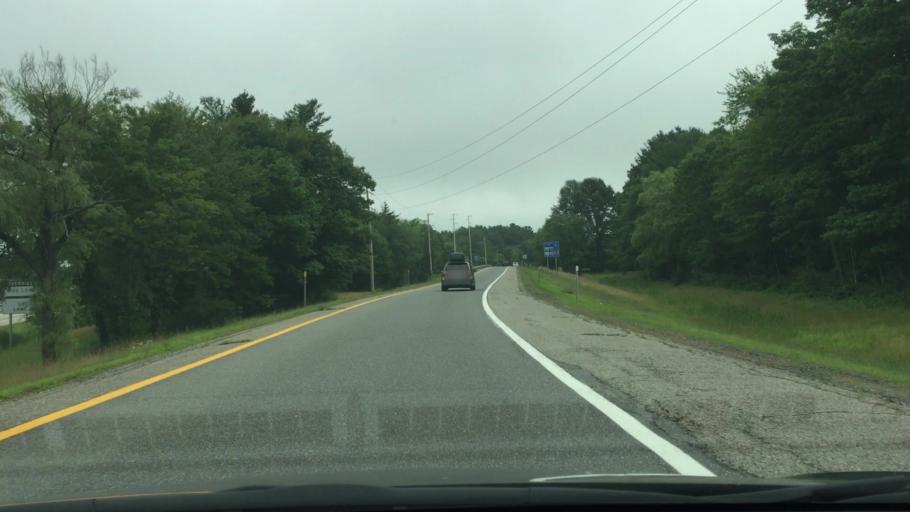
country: US
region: Maine
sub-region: York County
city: York Harbor
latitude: 43.1550
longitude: -70.6681
